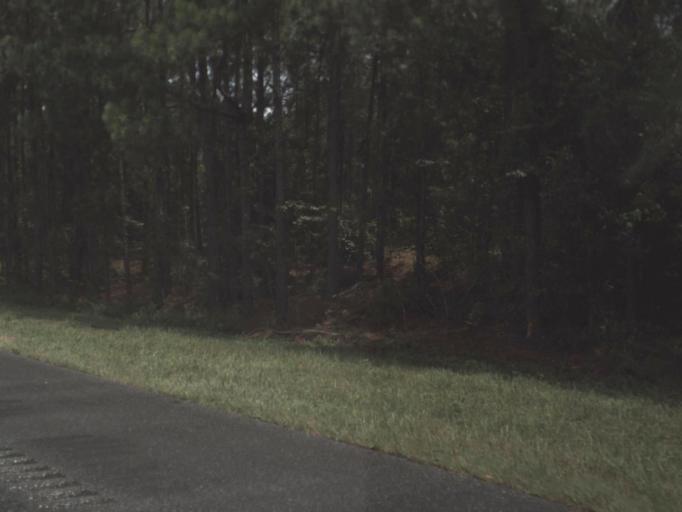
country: US
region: Florida
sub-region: Hernando County
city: Hill 'n Dale
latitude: 28.5385
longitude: -82.2369
